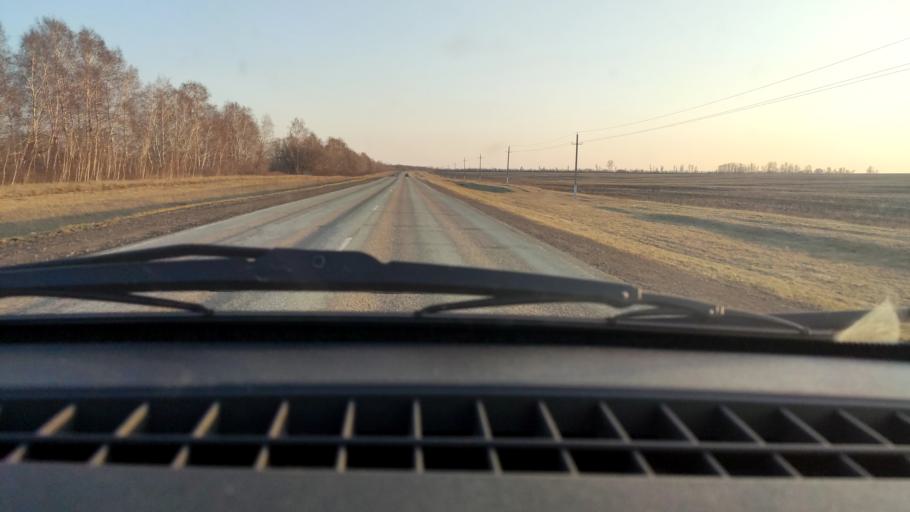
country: RU
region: Bashkortostan
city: Davlekanovo
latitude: 54.3391
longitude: 55.1714
